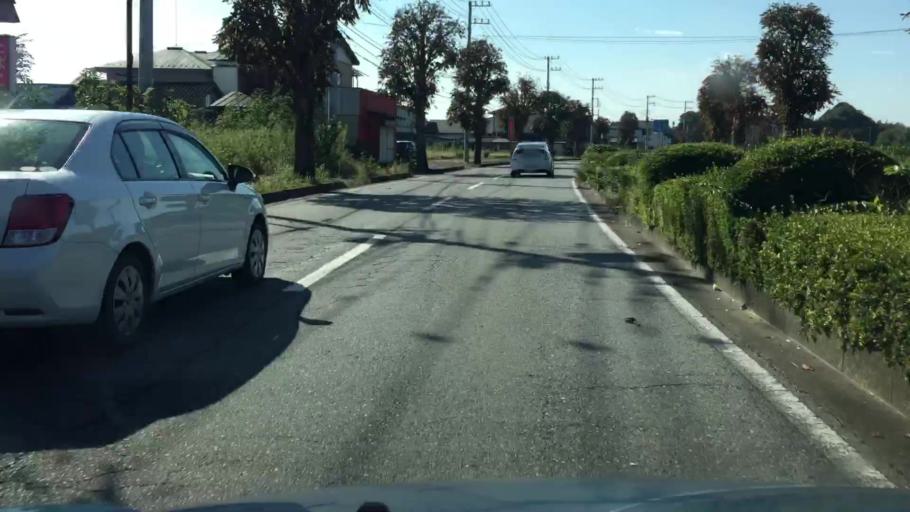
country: JP
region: Tochigi
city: Mooka
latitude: 36.5358
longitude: 139.9885
